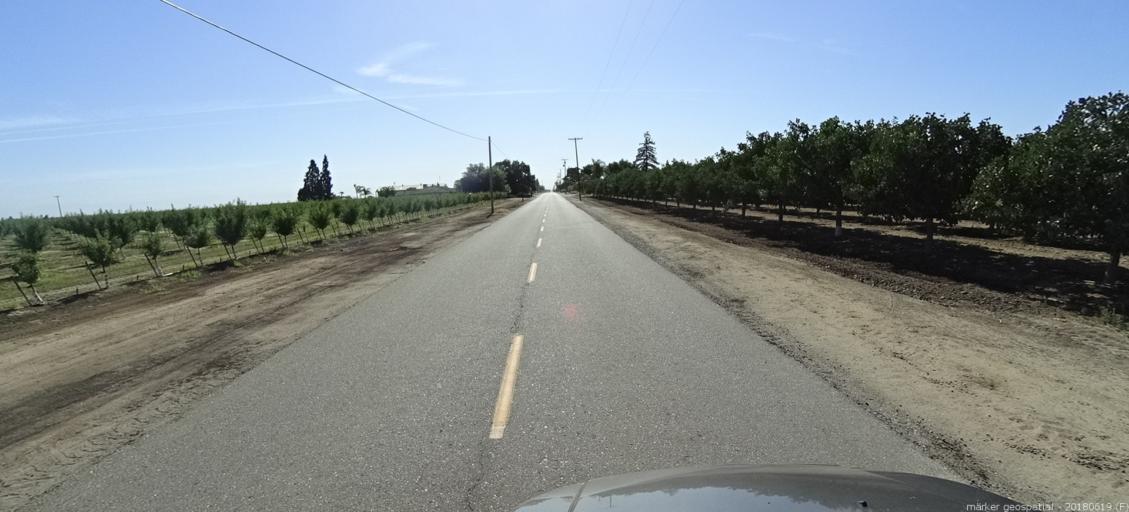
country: US
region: California
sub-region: Fresno County
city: Biola
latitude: 36.8296
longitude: -120.0721
